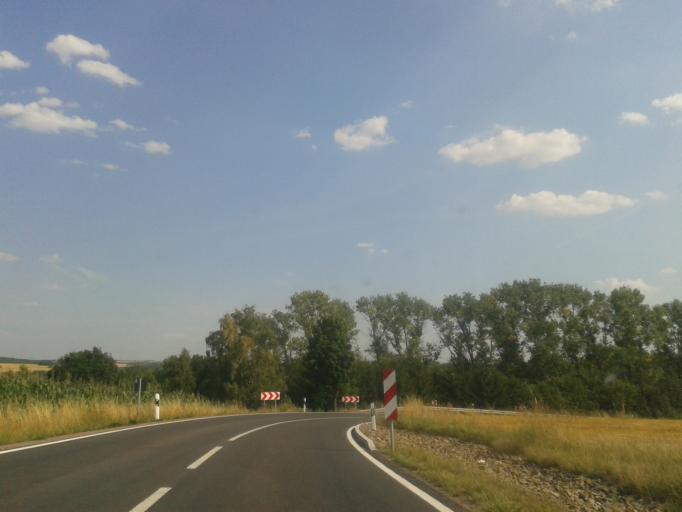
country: DE
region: Saxony
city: Nossen
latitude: 51.0250
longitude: 13.3246
